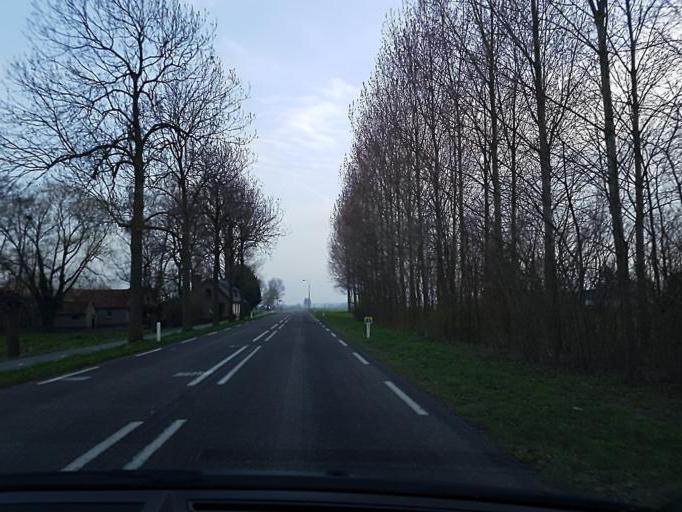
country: NL
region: Zeeland
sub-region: Gemeente Hulst
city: Hulst
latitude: 51.3343
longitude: 4.0338
